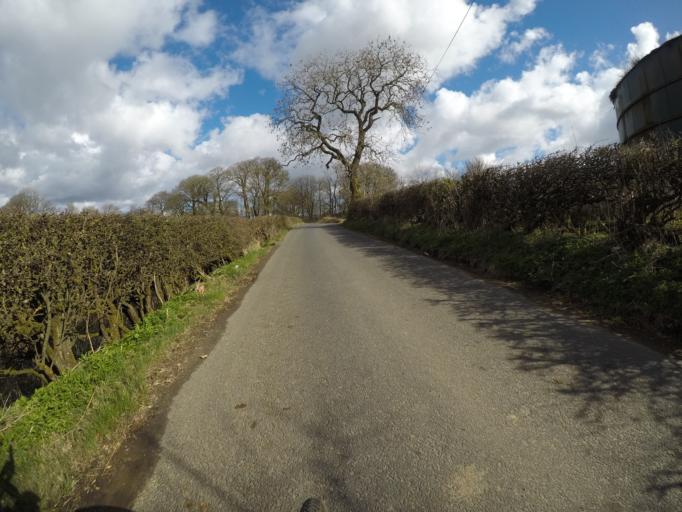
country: GB
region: Scotland
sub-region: North Ayrshire
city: Beith
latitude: 55.7284
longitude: -4.6070
